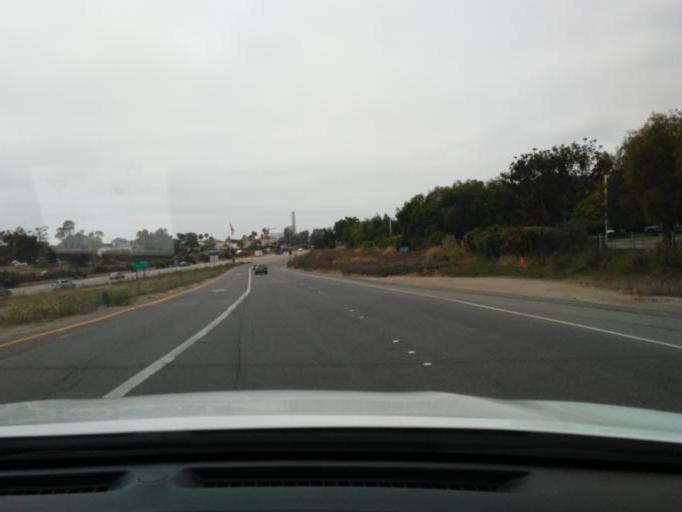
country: US
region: California
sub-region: San Diego County
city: Carlsbad
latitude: 33.1225
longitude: -117.3212
